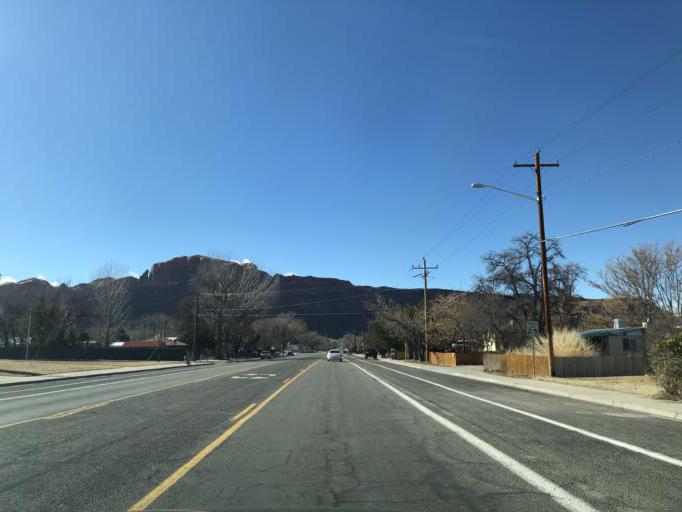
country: US
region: Utah
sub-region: Grand County
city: Moab
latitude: 38.5794
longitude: -109.5578
